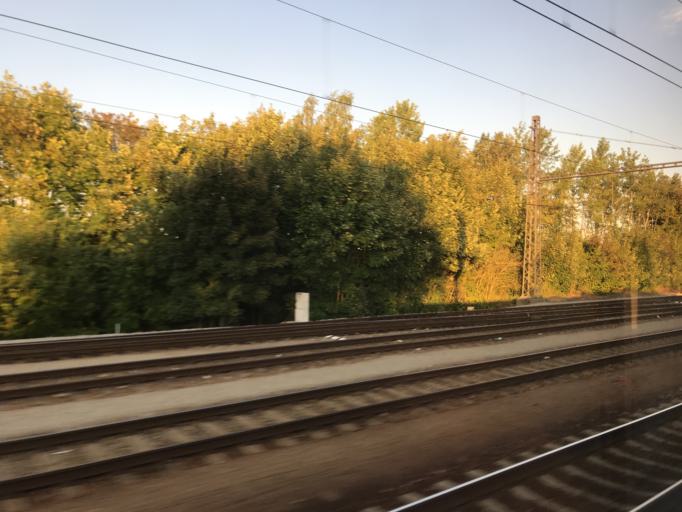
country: CZ
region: Central Bohemia
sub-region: Okres Benesov
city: Benesov
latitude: 49.7752
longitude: 14.6853
